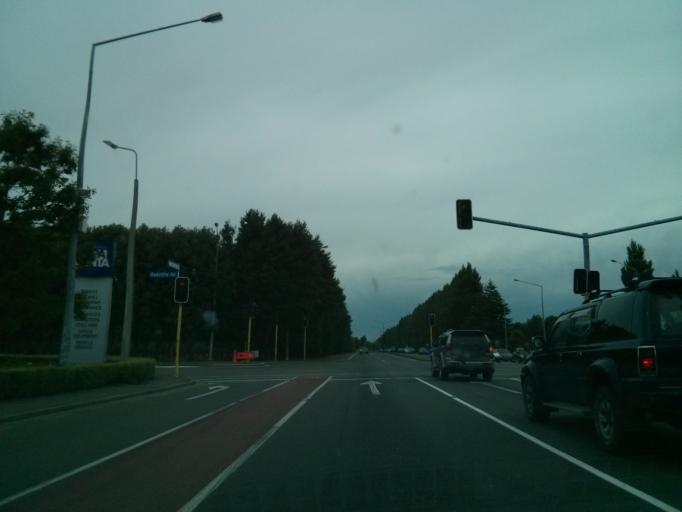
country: NZ
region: Canterbury
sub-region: Christchurch City
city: Christchurch
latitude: -43.4603
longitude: 172.6226
